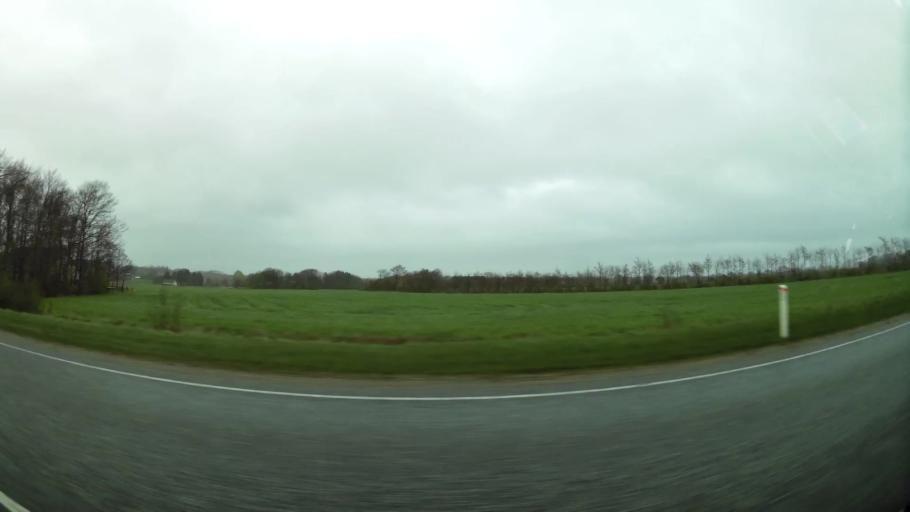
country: DK
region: Central Jutland
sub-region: Herning Kommune
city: Avlum
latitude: 56.2692
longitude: 8.7682
